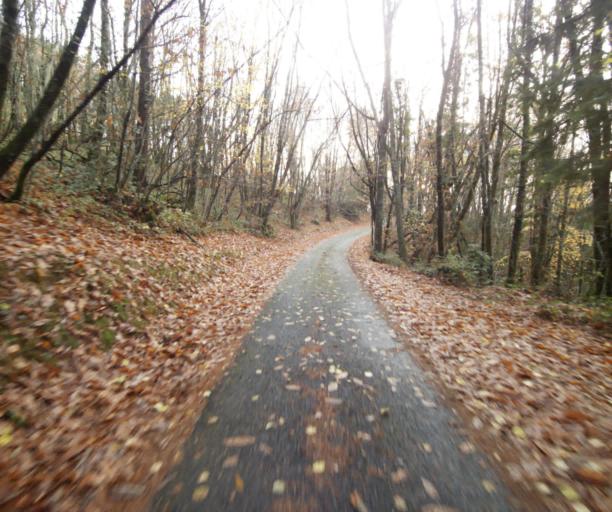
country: FR
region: Limousin
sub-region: Departement de la Correze
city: Cornil
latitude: 45.2026
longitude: 1.7010
